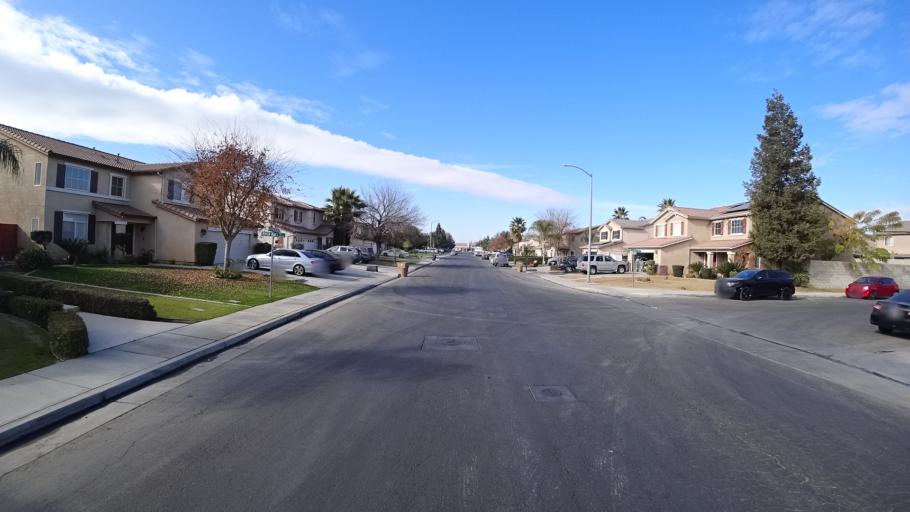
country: US
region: California
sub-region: Kern County
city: Greenacres
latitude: 35.2995
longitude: -119.1238
